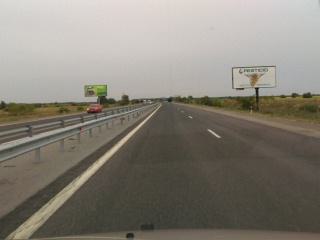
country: BG
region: Stara Zagora
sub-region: Obshtina Stara Zagora
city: Stara Zagora
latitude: 42.3243
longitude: 25.6058
